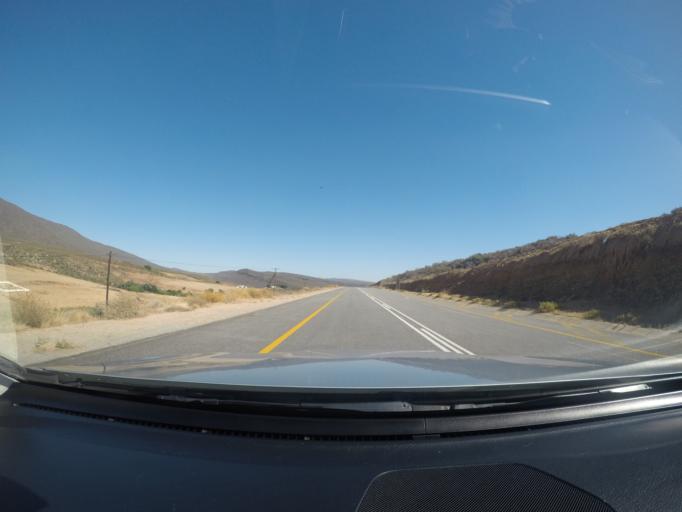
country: ZA
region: Western Cape
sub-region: West Coast District Municipality
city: Clanwilliam
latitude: -32.2406
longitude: 18.8514
